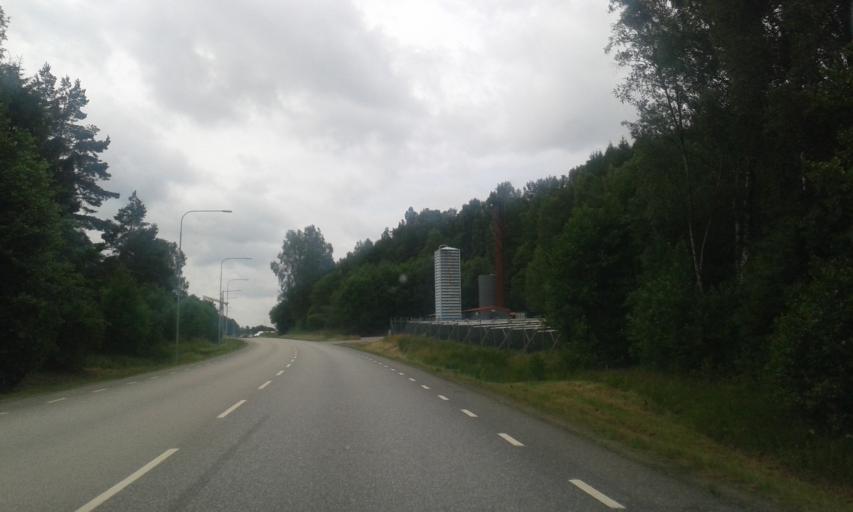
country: SE
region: Vaestra Goetaland
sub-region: Kungalvs Kommun
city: Kungalv
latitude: 57.8668
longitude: 11.8995
